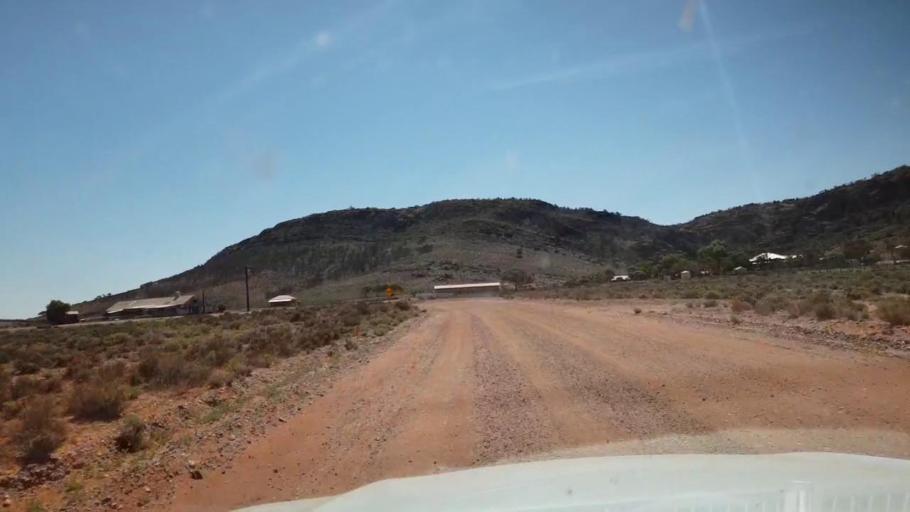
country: AU
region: South Australia
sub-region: Whyalla
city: Whyalla
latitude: -32.6868
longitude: 137.1262
